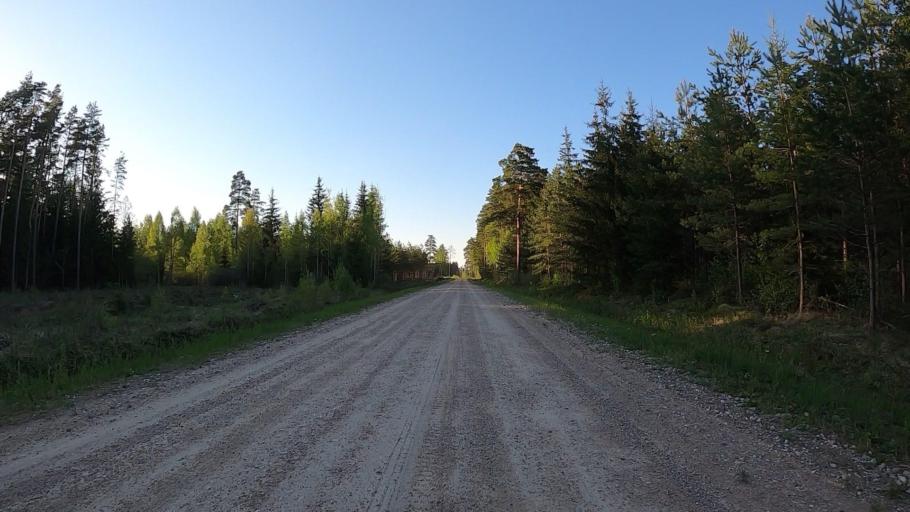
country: LV
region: Kekava
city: Kekava
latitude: 56.7659
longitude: 24.2227
